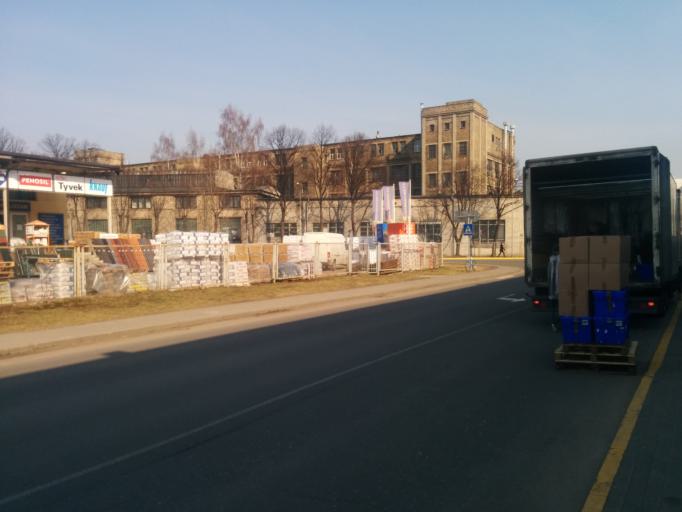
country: LV
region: Riga
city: Riga
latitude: 56.9669
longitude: 24.1610
